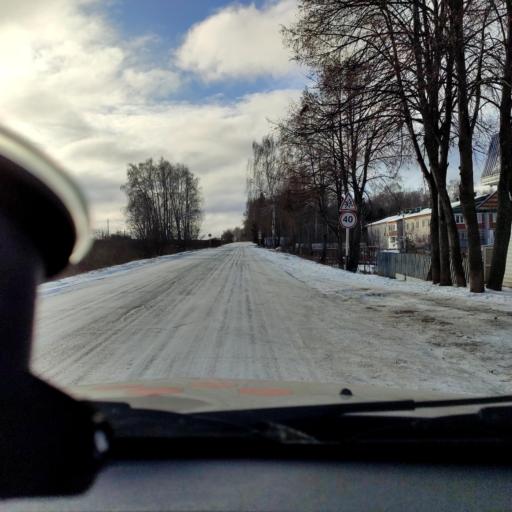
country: RU
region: Bashkortostan
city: Avdon
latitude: 54.7855
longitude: 55.7598
